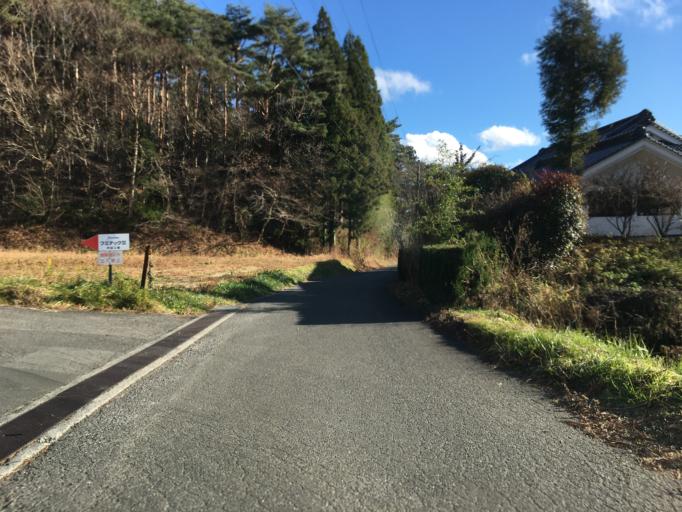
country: JP
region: Fukushima
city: Ishikawa
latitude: 37.2638
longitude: 140.5585
